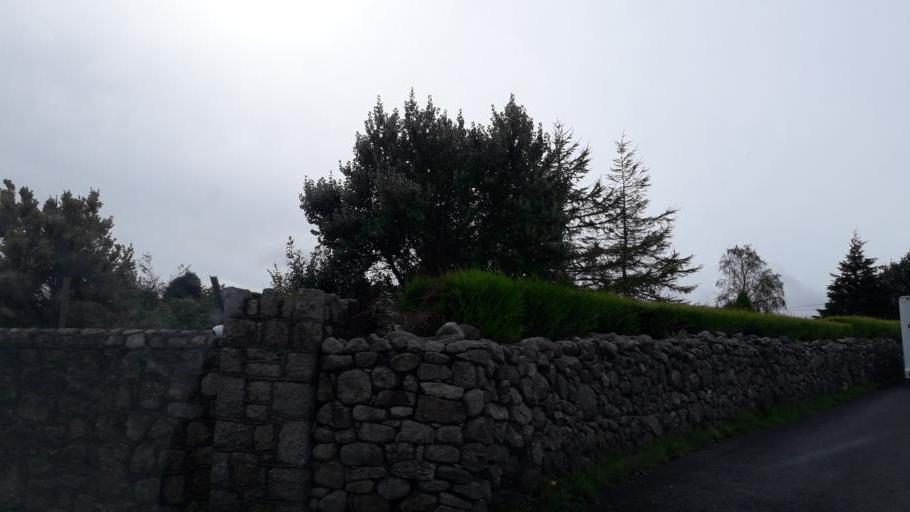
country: IE
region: Leinster
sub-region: Wicklow
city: Enniskerry
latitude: 53.2238
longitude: -6.2074
